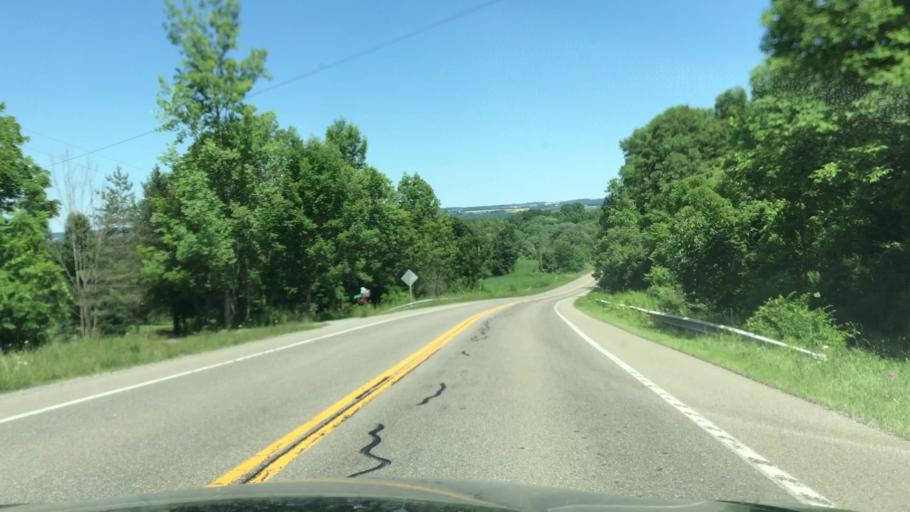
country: US
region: New York
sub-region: Livingston County
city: Mount Morris
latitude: 42.7561
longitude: -77.9021
